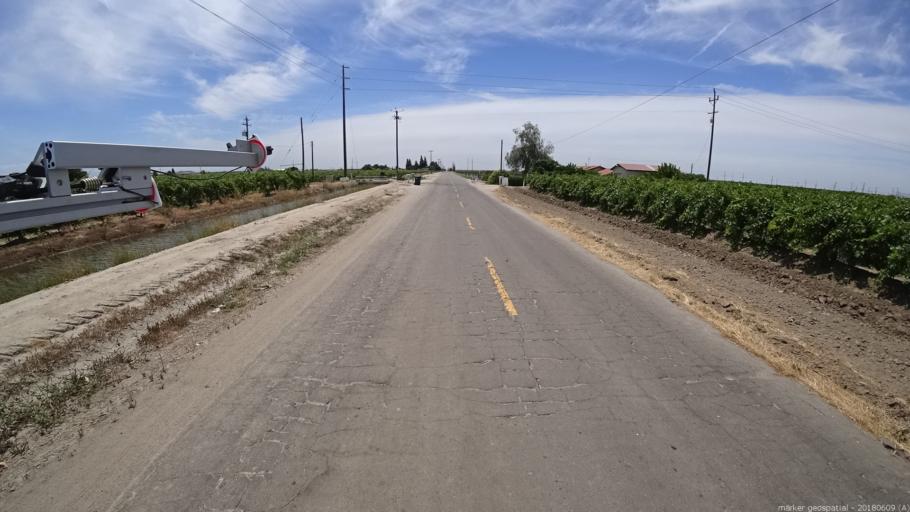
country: US
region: California
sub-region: Madera County
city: Parkwood
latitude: 36.9166
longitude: -120.0506
